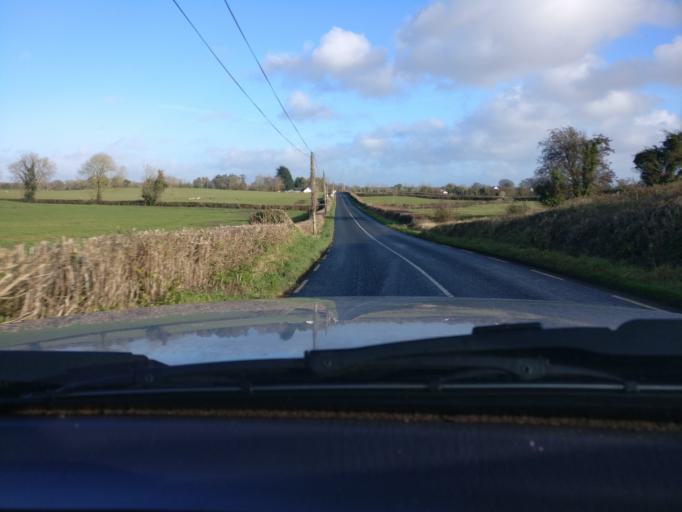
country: IE
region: Leinster
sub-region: An Iarmhi
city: Kilbeggan
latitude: 53.4703
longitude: -7.4723
